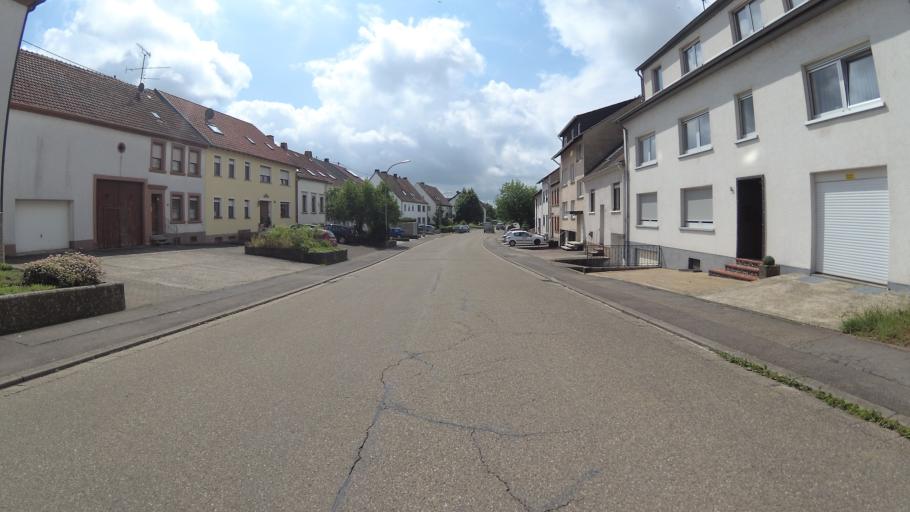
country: DE
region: Saarland
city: Kleinblittersdorf
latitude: 49.1404
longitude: 7.0574
